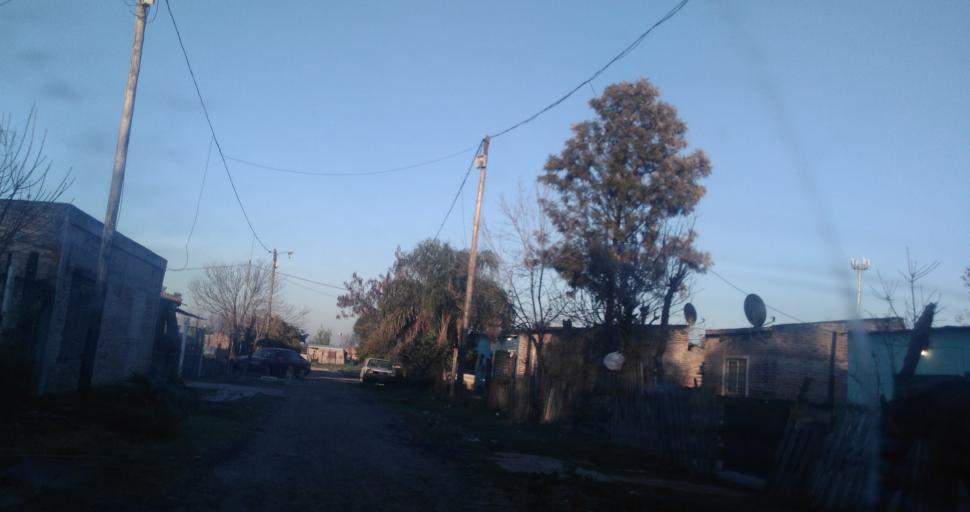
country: AR
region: Chaco
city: Resistencia
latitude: -27.4599
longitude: -59.0240
